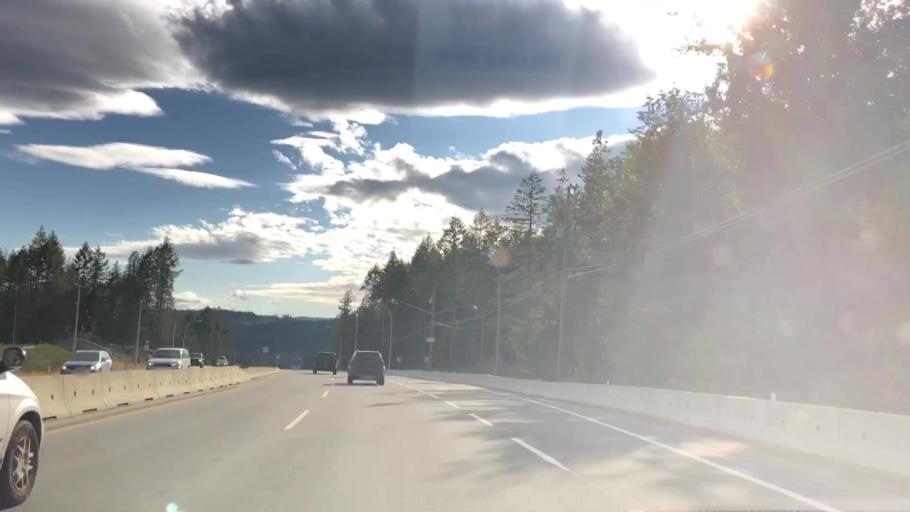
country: CA
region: British Columbia
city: Langford
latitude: 48.5671
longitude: -123.5605
